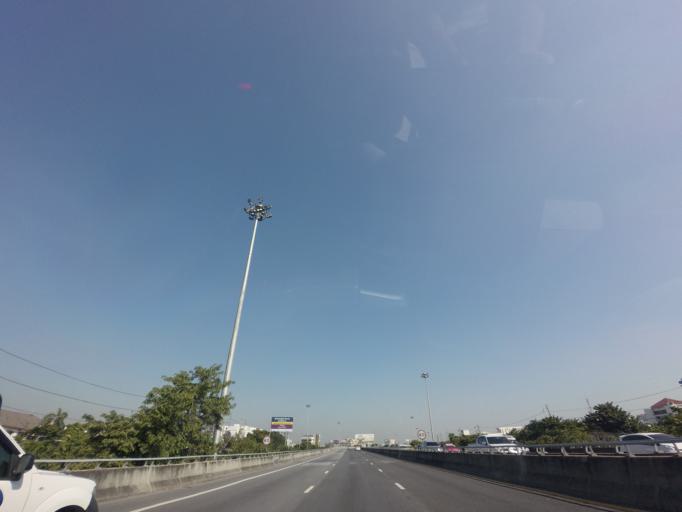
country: TH
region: Bangkok
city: Wang Thonglang
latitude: 13.7825
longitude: 100.6078
